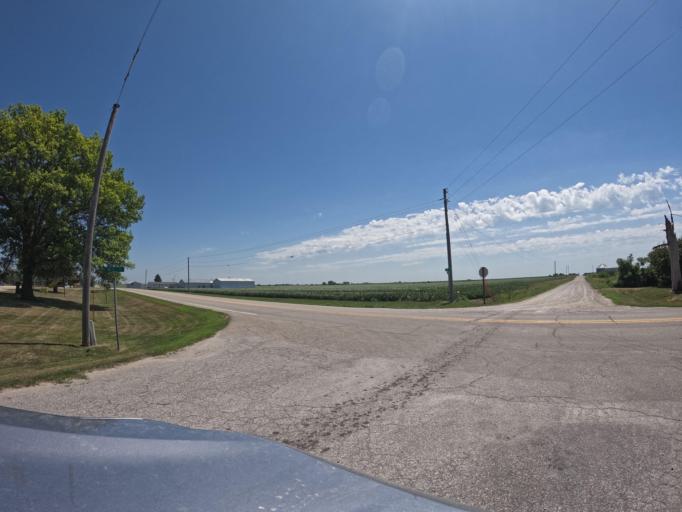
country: US
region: Iowa
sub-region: Keokuk County
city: Sigourney
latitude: 41.4523
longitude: -92.3358
